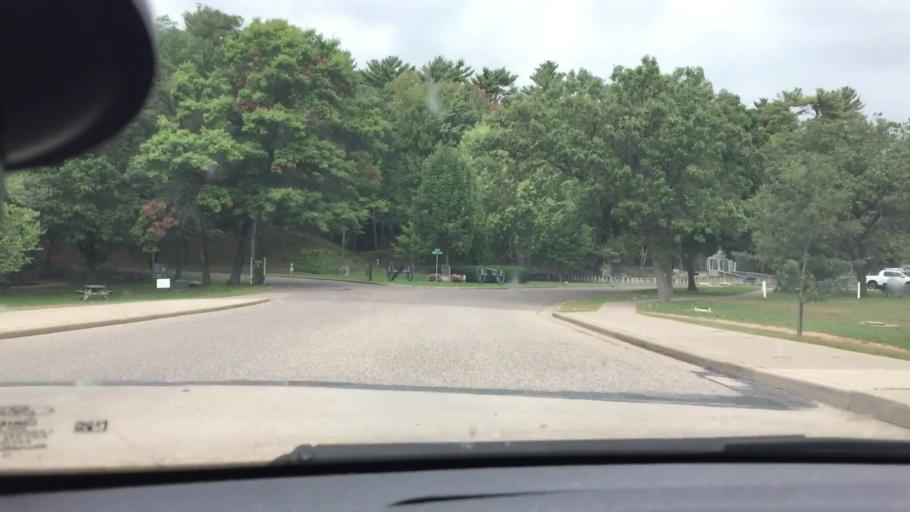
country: US
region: Wisconsin
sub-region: Chippewa County
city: Chippewa Falls
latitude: 44.9475
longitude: -91.4004
